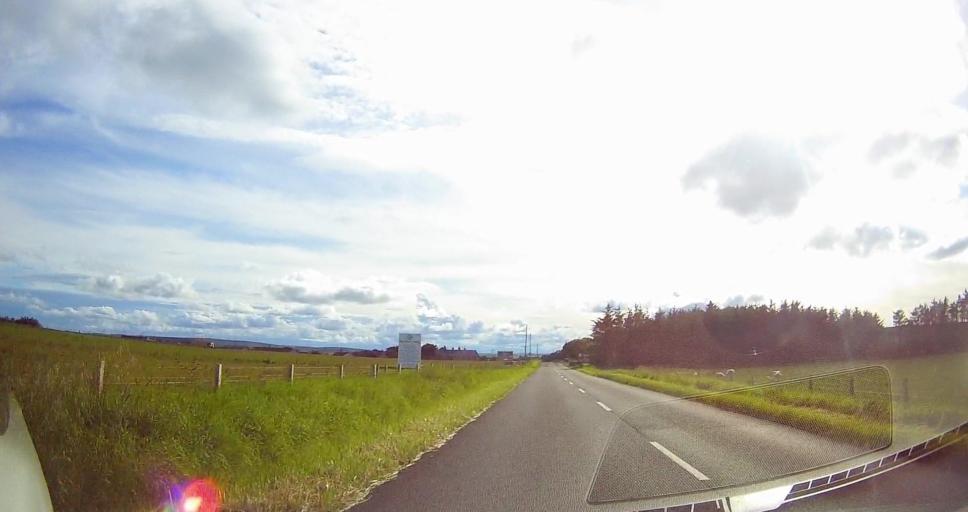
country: GB
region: Scotland
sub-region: Highland
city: Thurso
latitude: 58.6251
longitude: -3.3360
